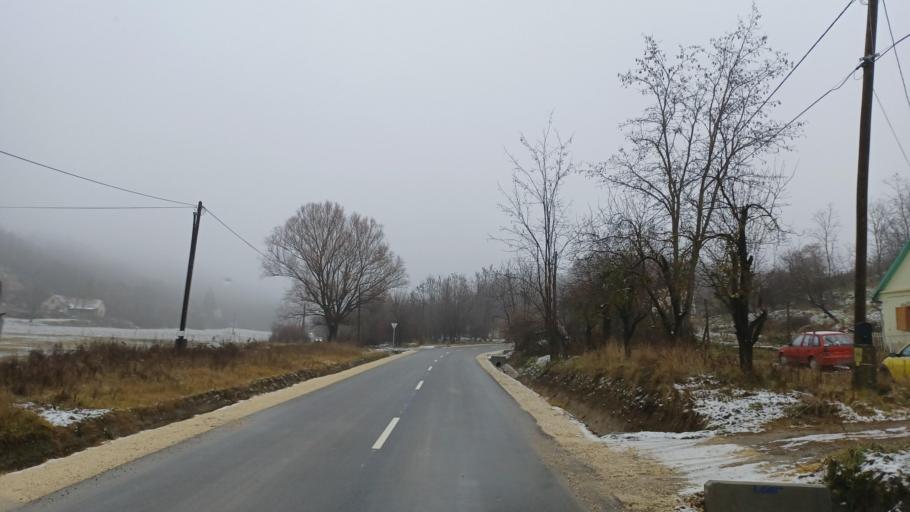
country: HU
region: Tolna
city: Gyonk
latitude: 46.5718
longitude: 18.4737
